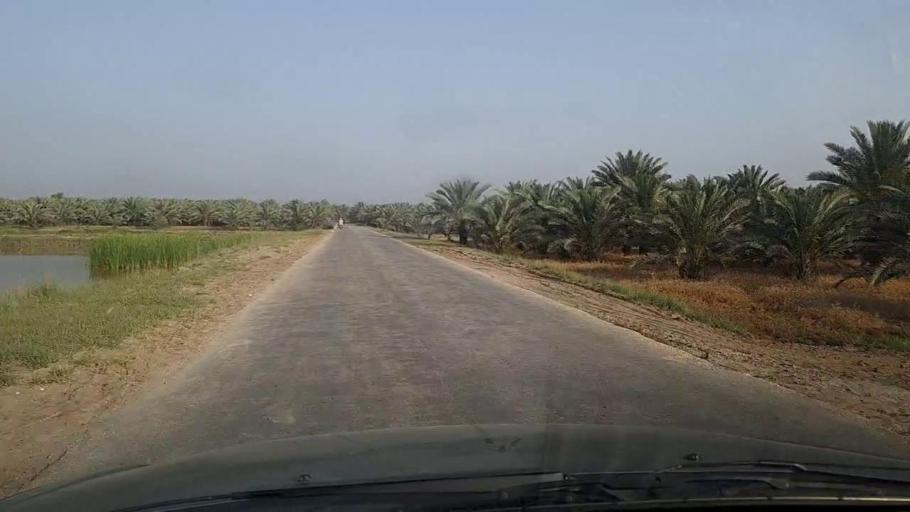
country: PK
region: Sindh
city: Pir jo Goth
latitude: 27.5661
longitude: 68.6429
